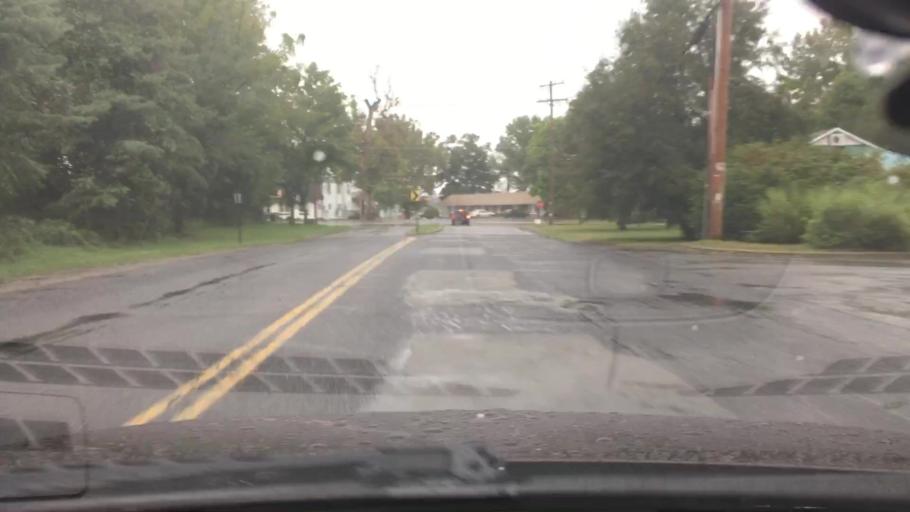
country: US
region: New York
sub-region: Dutchess County
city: Myers Corner
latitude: 41.6288
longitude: -73.8746
